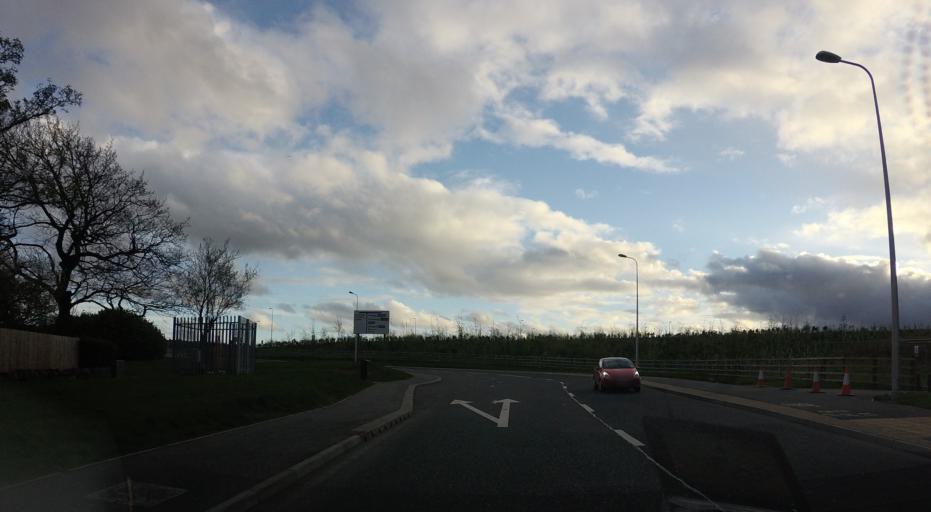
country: GB
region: Scotland
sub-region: Edinburgh
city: Queensferry
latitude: 55.9863
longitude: -3.4198
